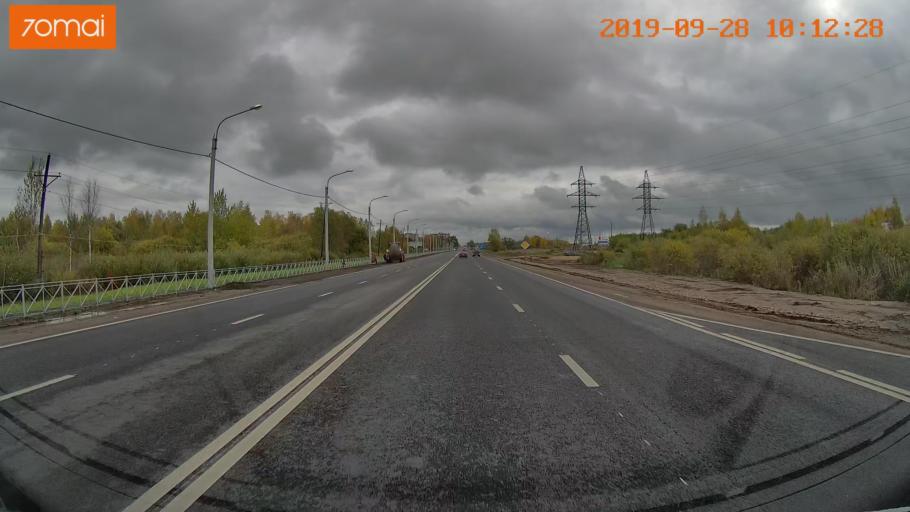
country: RU
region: Jaroslavl
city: Yaroslavl
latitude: 57.5422
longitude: 39.9587
